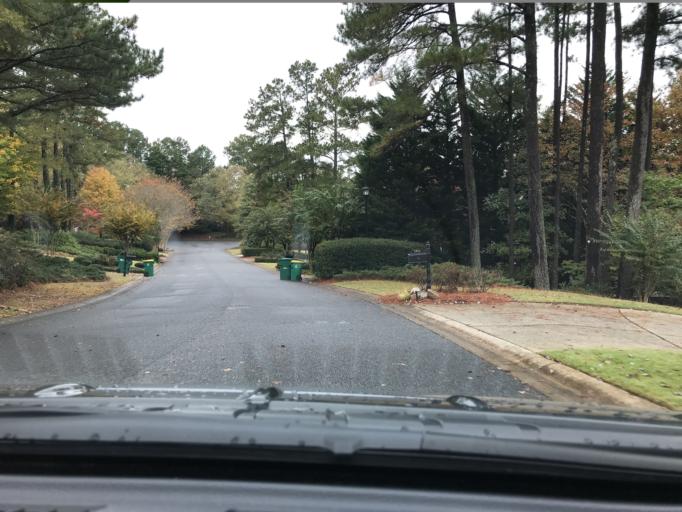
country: US
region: Georgia
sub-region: Fulton County
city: Johns Creek
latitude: 34.0158
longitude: -84.2494
